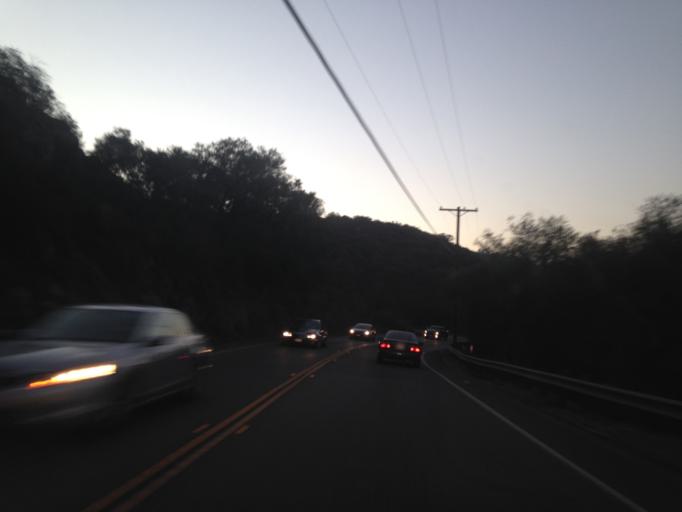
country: US
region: California
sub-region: San Diego County
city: Bonsall
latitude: 33.2543
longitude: -117.2062
